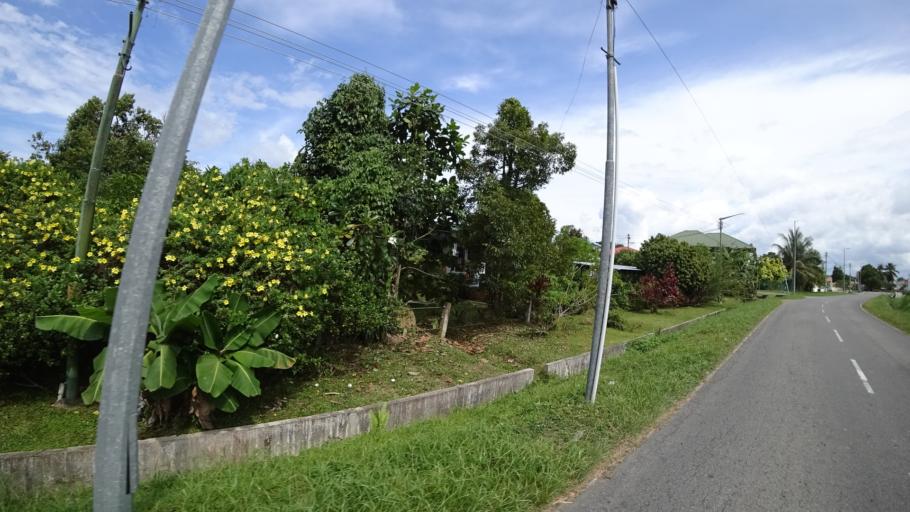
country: BN
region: Brunei and Muara
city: Bandar Seri Begawan
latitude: 4.8909
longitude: 114.8420
